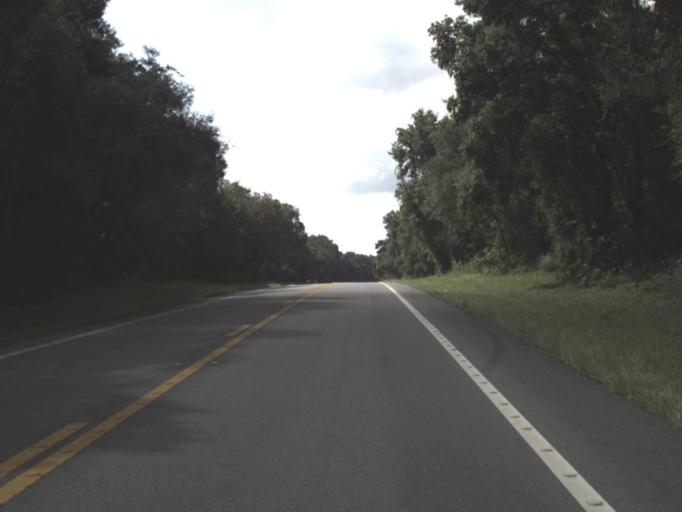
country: US
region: Florida
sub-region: Citrus County
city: Hernando
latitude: 28.9330
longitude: -82.3953
